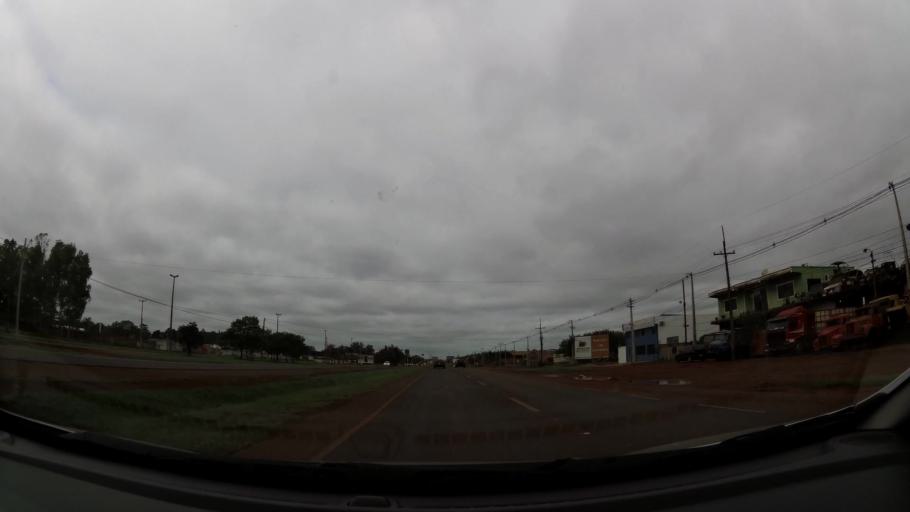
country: PY
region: Alto Parana
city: Presidente Franco
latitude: -25.4909
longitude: -54.7643
